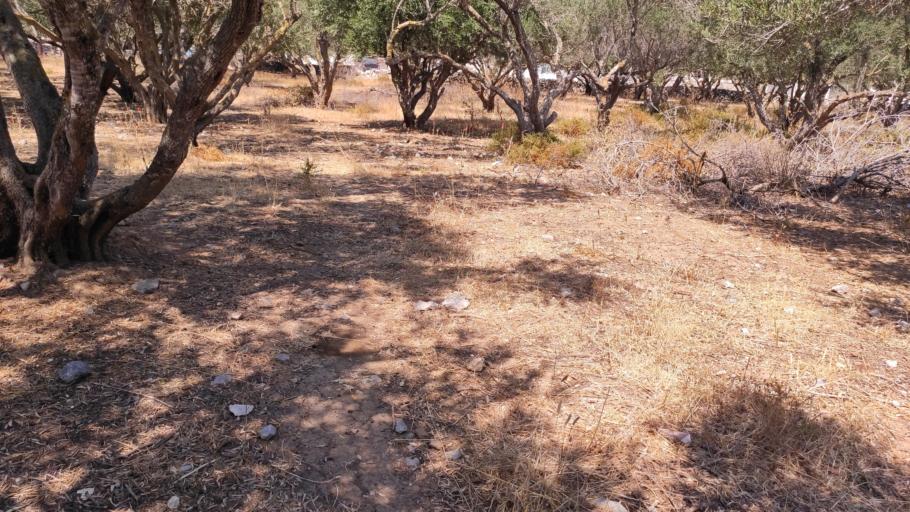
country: GR
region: South Aegean
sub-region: Nomos Dodekanisou
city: Pylion
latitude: 36.9334
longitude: 27.1351
